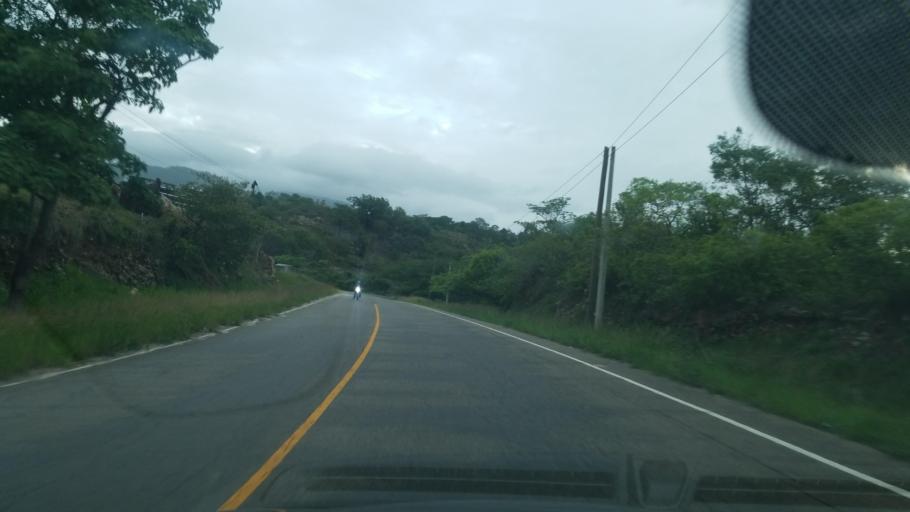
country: HN
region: Ocotepeque
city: Sinuapa
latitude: 14.4996
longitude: -89.2204
